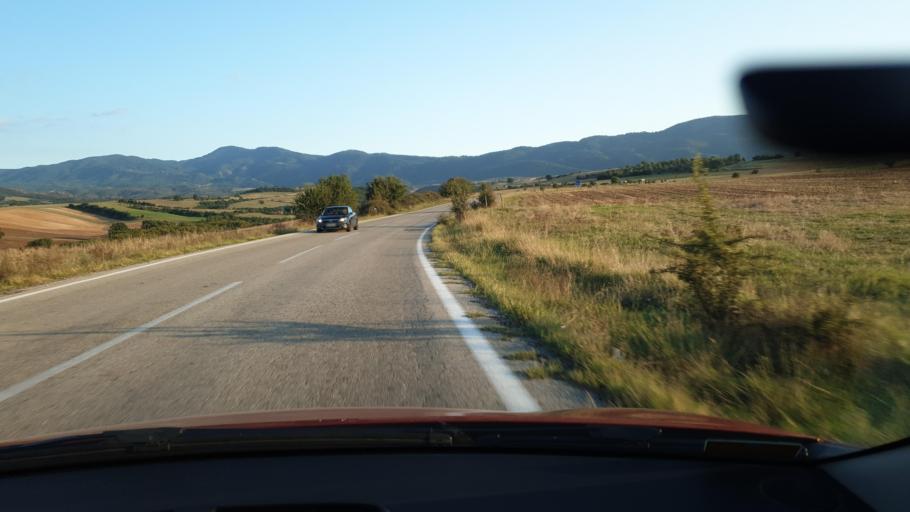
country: GR
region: Central Macedonia
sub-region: Nomos Thessalonikis
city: Nea Apollonia
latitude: 40.5326
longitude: 23.4705
